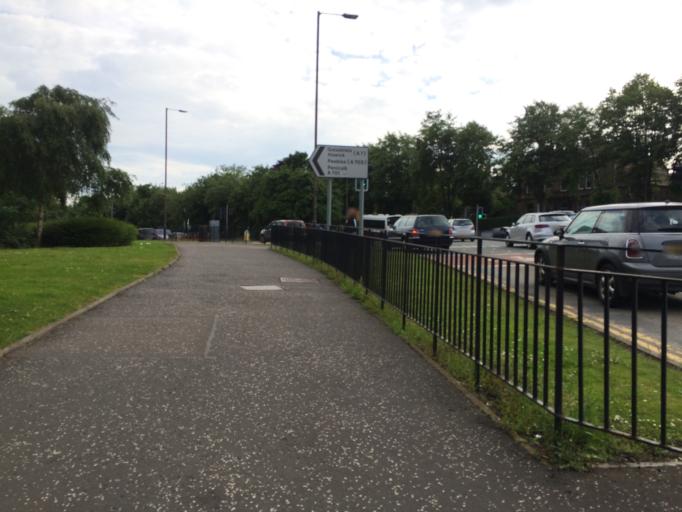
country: GB
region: Scotland
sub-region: Edinburgh
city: Edinburgh
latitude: 55.9267
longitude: -3.1662
